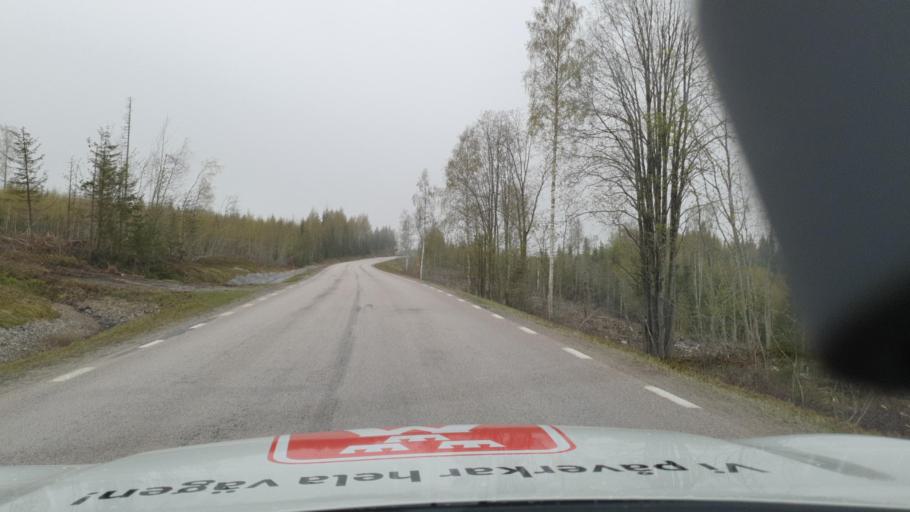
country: SE
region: Vaesterbotten
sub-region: Vannas Kommun
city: Vaennaes
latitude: 63.7903
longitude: 19.8222
